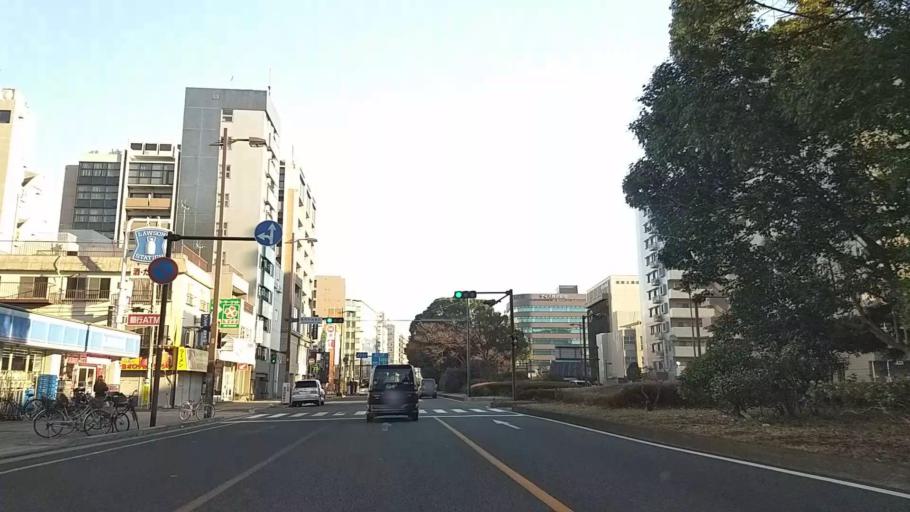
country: JP
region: Kanagawa
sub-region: Kawasaki-shi
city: Kawasaki
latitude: 35.5059
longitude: 139.6794
